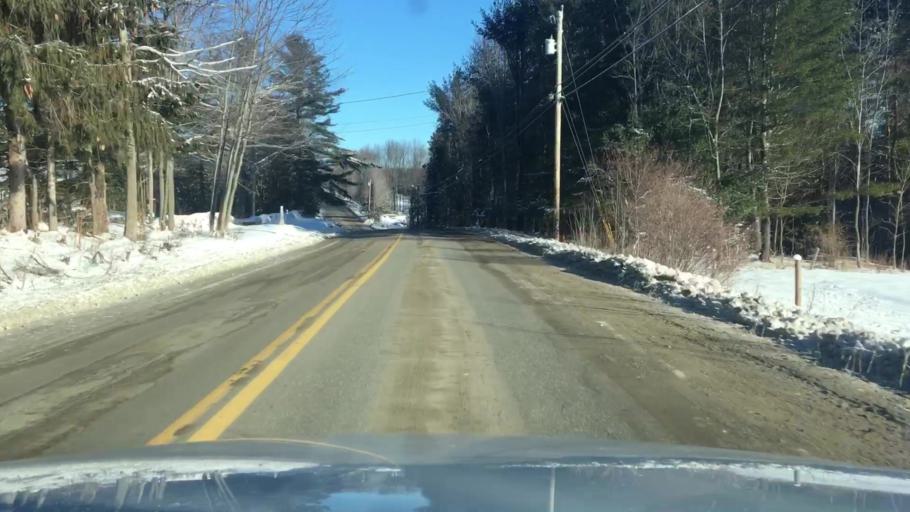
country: US
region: Maine
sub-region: Kennebec County
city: Mount Vernon
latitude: 44.4736
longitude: -69.9729
